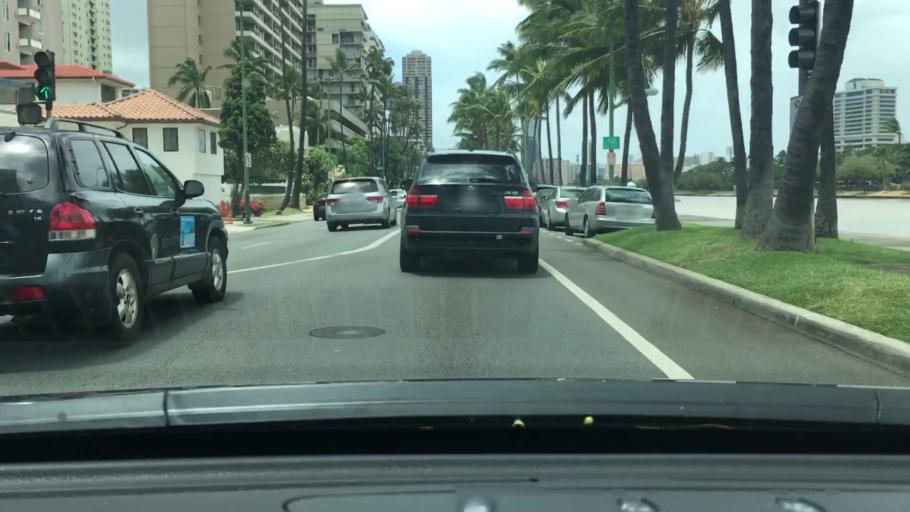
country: US
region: Hawaii
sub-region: Honolulu County
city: Honolulu
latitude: 21.2828
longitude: -157.8271
